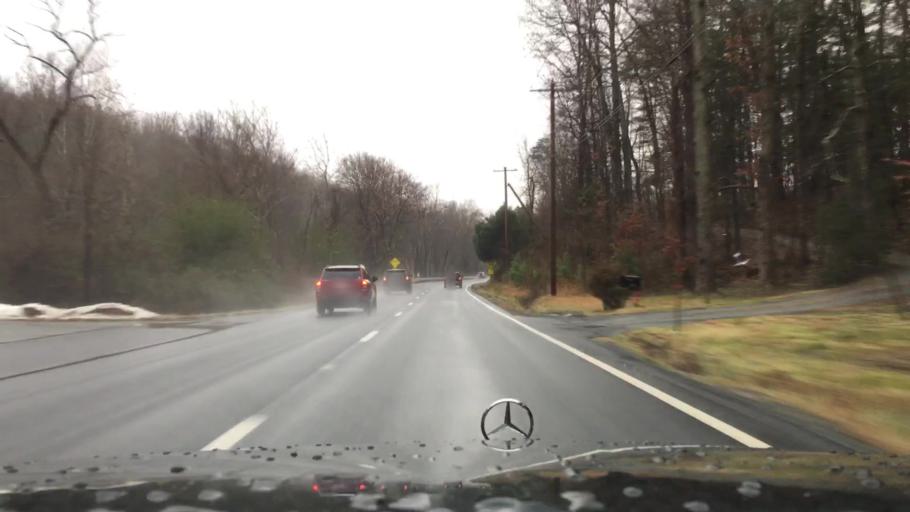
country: US
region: Virginia
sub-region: Albemarle County
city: Crozet
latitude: 37.9332
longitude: -78.6735
